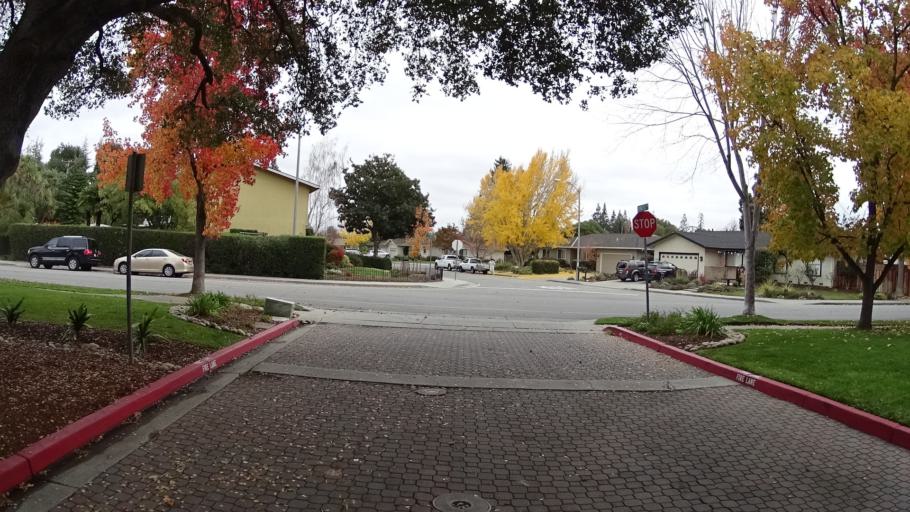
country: US
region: California
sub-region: Santa Clara County
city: Sunnyvale
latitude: 37.3557
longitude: -122.0459
